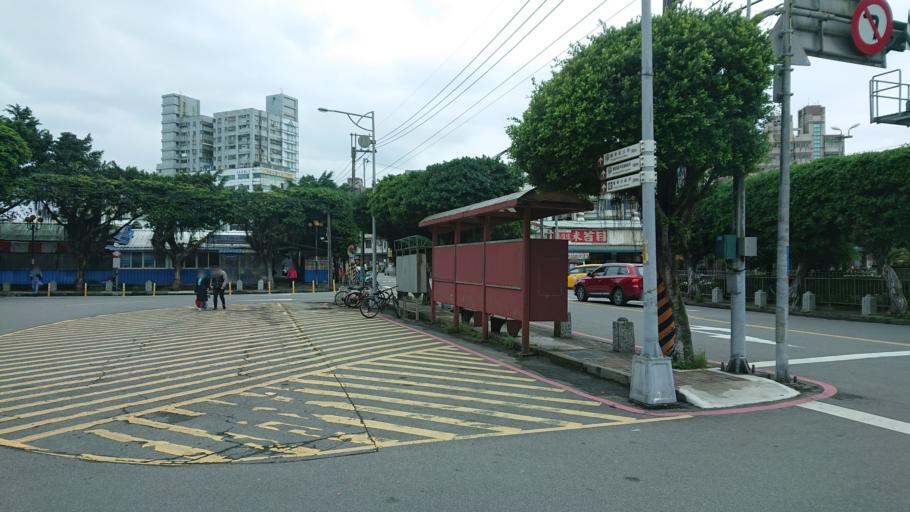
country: TW
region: Taiwan
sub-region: Taoyuan
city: Taoyuan
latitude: 24.9550
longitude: 121.3549
